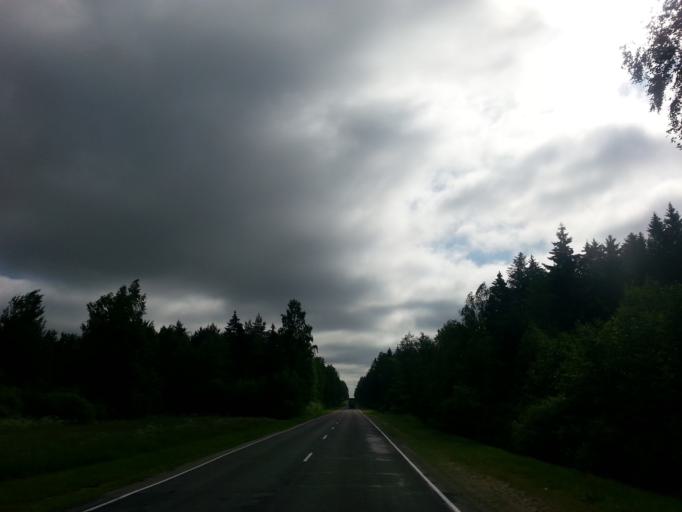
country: BY
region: Vitebsk
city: Mosar
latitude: 55.0825
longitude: 27.4550
